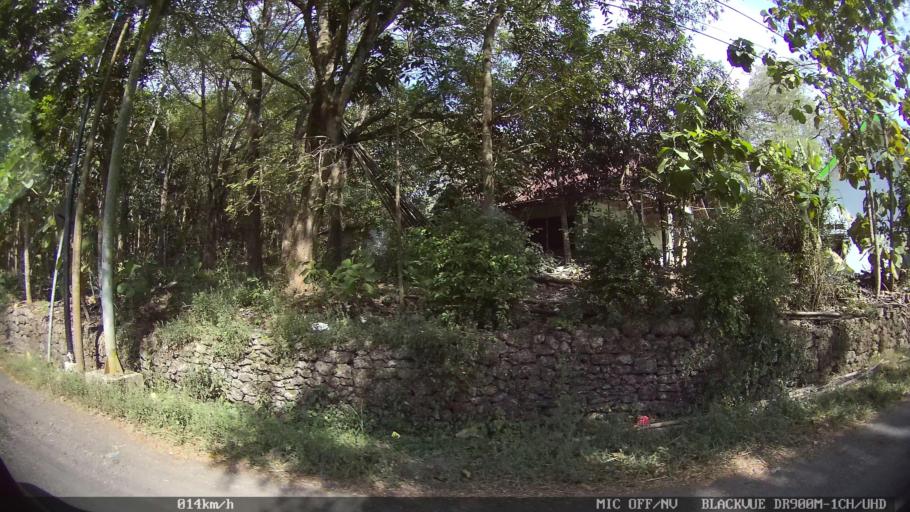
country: ID
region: Daerah Istimewa Yogyakarta
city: Kasihan
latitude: -7.8497
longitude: 110.2985
